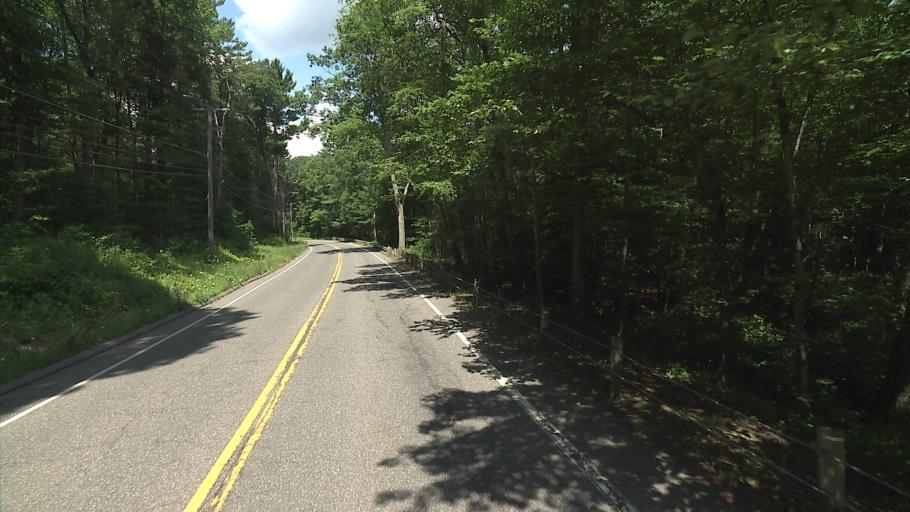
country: US
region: Connecticut
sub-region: Litchfield County
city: Canaan
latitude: 41.8689
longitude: -73.3292
